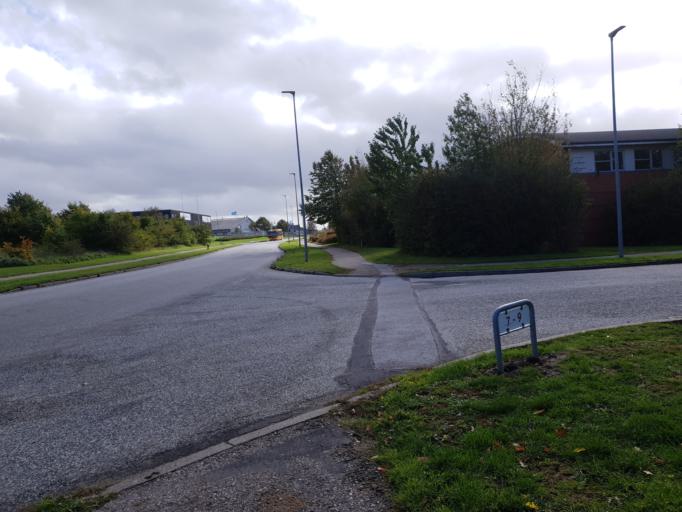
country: DK
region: South Denmark
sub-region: Kolding Kommune
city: Kolding
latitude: 55.5372
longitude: 9.4744
